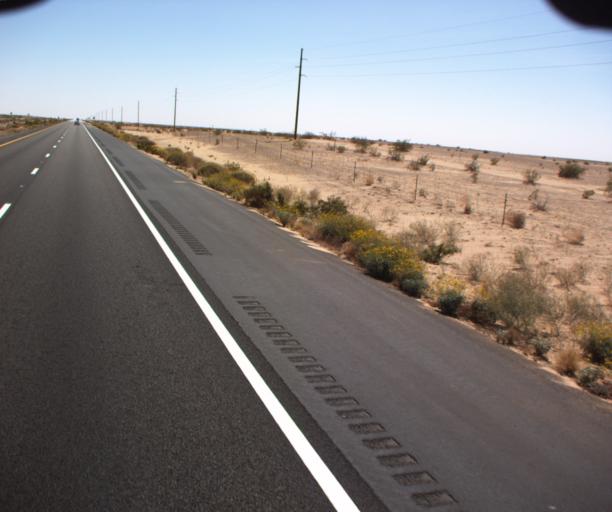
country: US
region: Arizona
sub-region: Yuma County
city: Somerton
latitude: 32.5318
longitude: -114.5622
